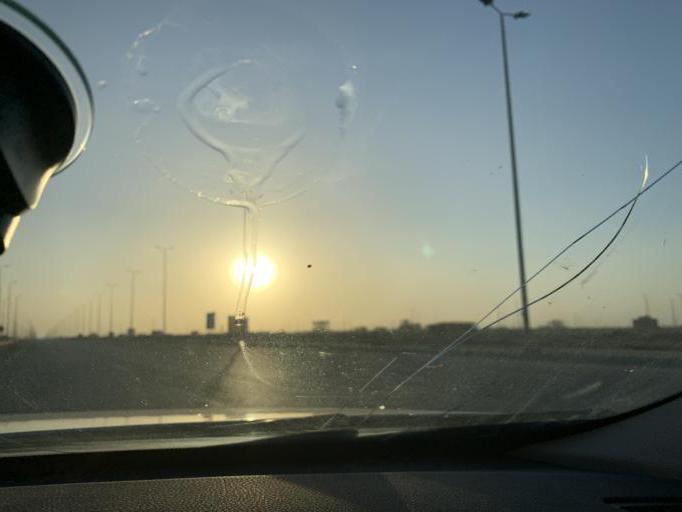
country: EG
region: Muhafazat al Qalyubiyah
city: Al Khankah
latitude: 30.0269
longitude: 31.5812
